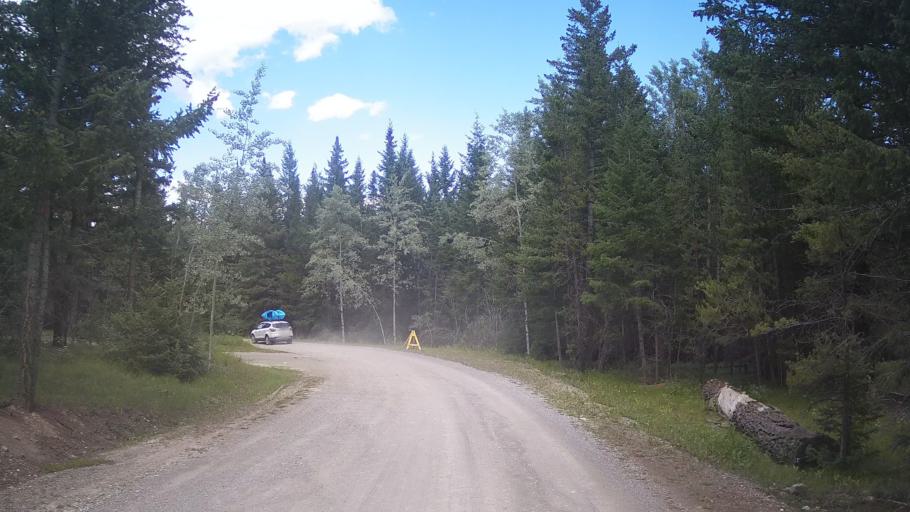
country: CA
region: British Columbia
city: Lillooet
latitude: 51.3109
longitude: -121.8240
